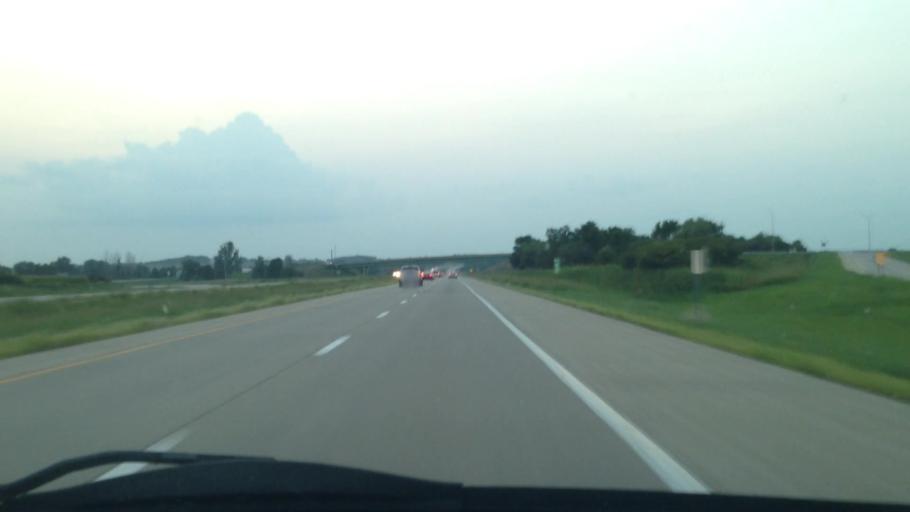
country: US
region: Iowa
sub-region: Black Hawk County
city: La Porte City
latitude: 42.4108
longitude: -92.1680
